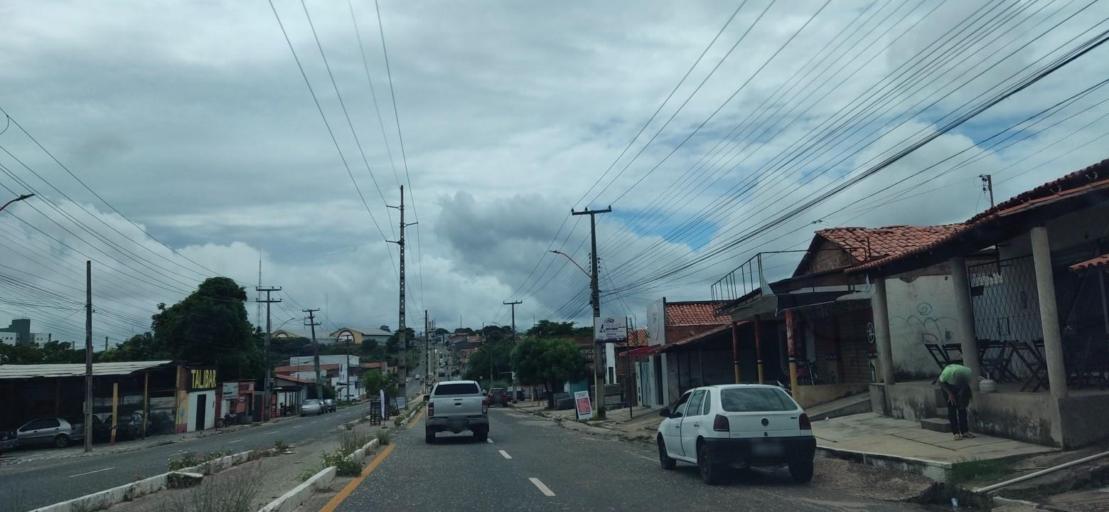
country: BR
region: Piaui
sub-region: Teresina
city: Teresina
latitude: -5.0597
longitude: -42.7540
